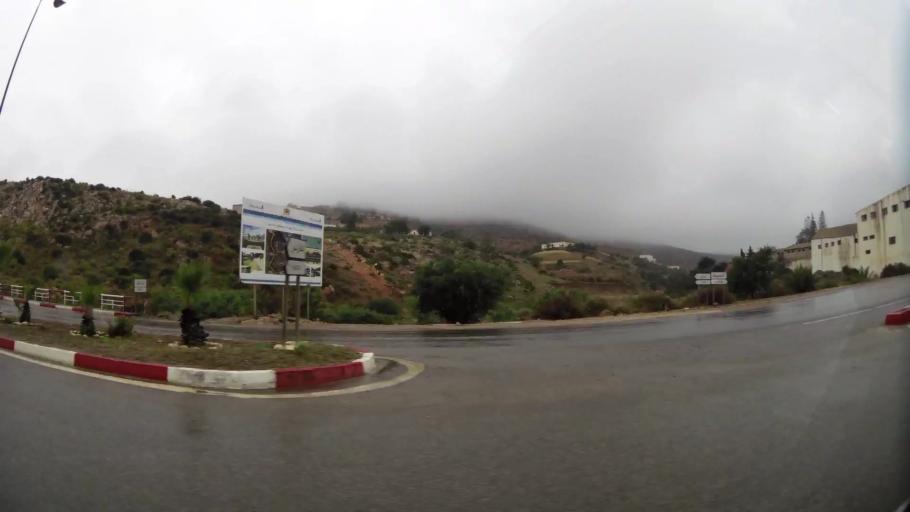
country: MA
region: Taza-Al Hoceima-Taounate
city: Al Hoceima
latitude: 35.2172
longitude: -3.9204
